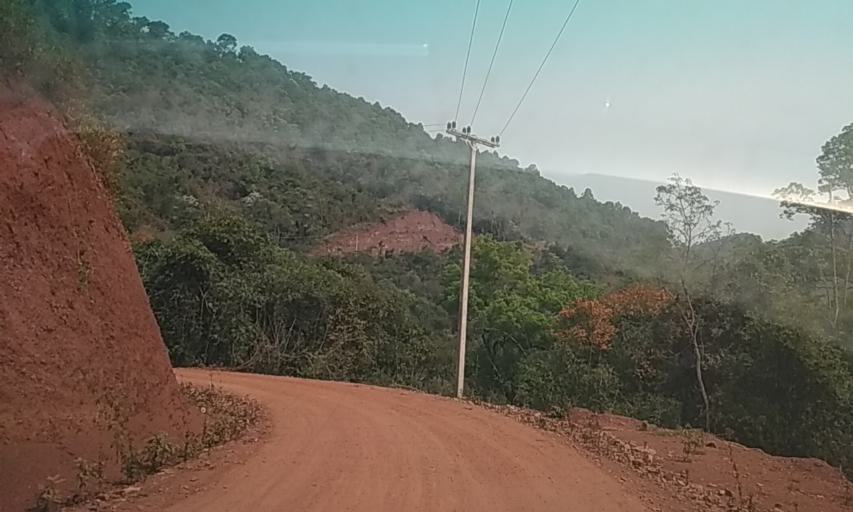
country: VN
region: Huyen Dien Bien
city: Dien Bien Phu
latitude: 21.4538
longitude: 102.7676
